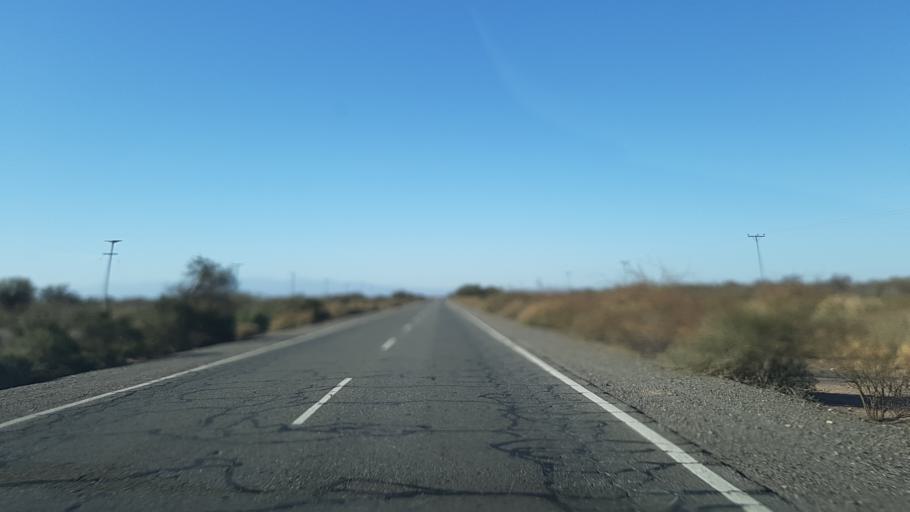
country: AR
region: San Juan
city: Caucete
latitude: -31.6239
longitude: -67.7361
